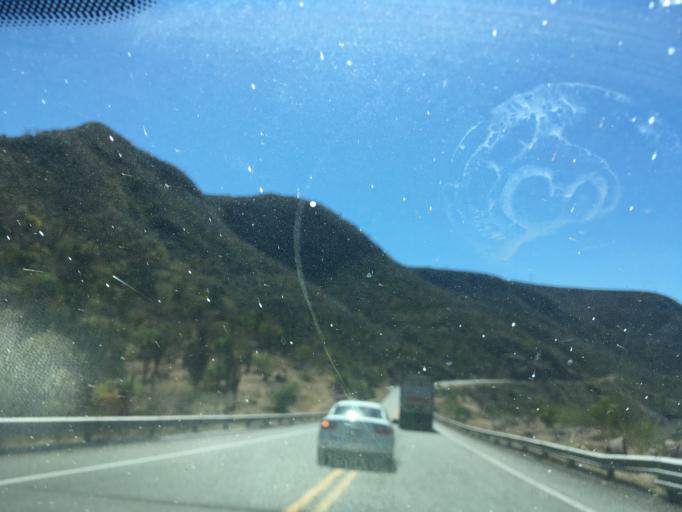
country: MX
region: Michoacan
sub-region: Arteaga
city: Las Canas
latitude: 18.4527
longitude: -101.9325
